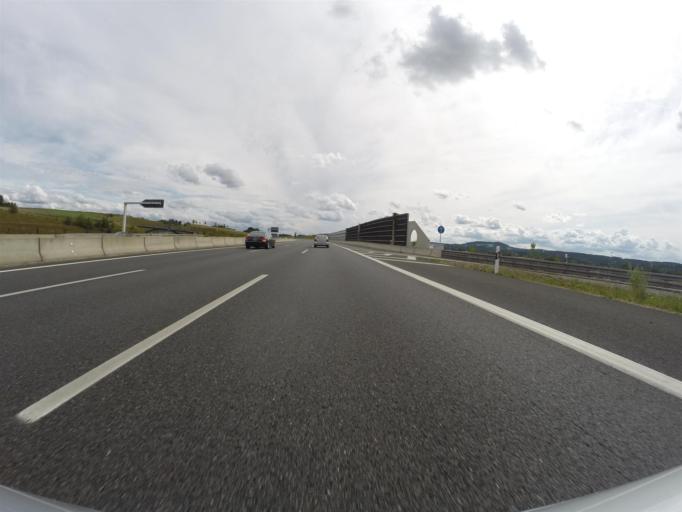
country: DE
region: Bavaria
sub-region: Upper Franconia
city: Bayreuth
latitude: 49.9294
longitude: 11.6022
